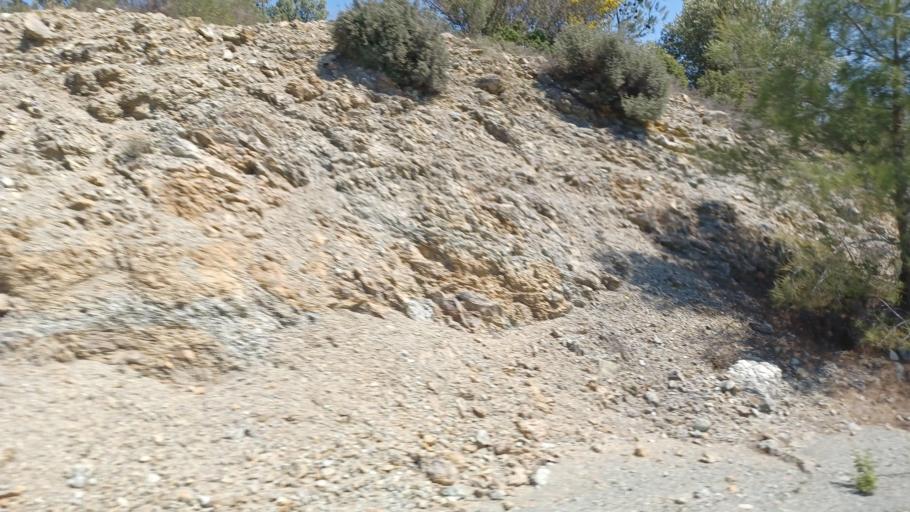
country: CY
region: Limassol
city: Parekklisha
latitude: 34.8009
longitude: 33.1367
